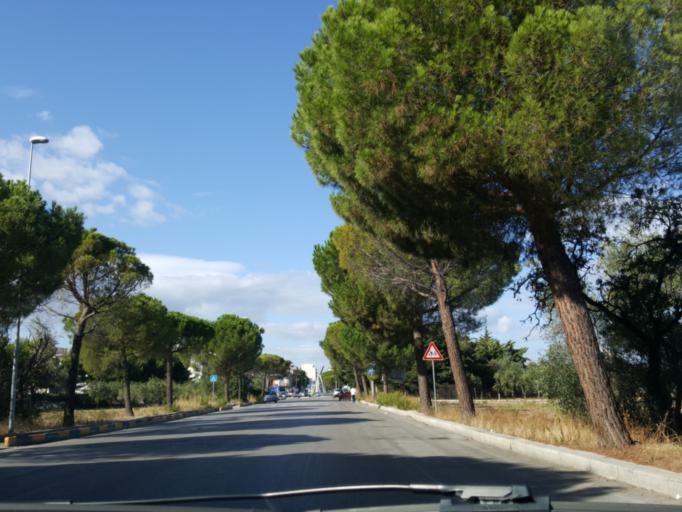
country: IT
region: Apulia
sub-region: Provincia di Bari
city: Triggiano
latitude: 41.0687
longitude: 16.9309
